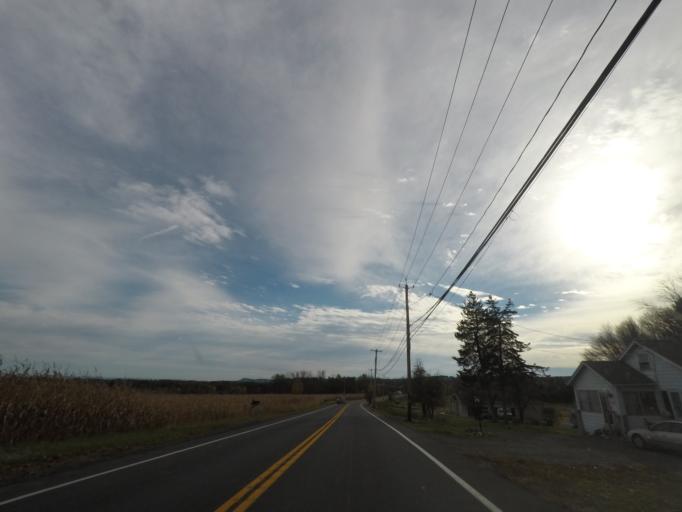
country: US
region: New York
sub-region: Albany County
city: Voorheesville
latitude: 42.6367
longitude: -73.9023
